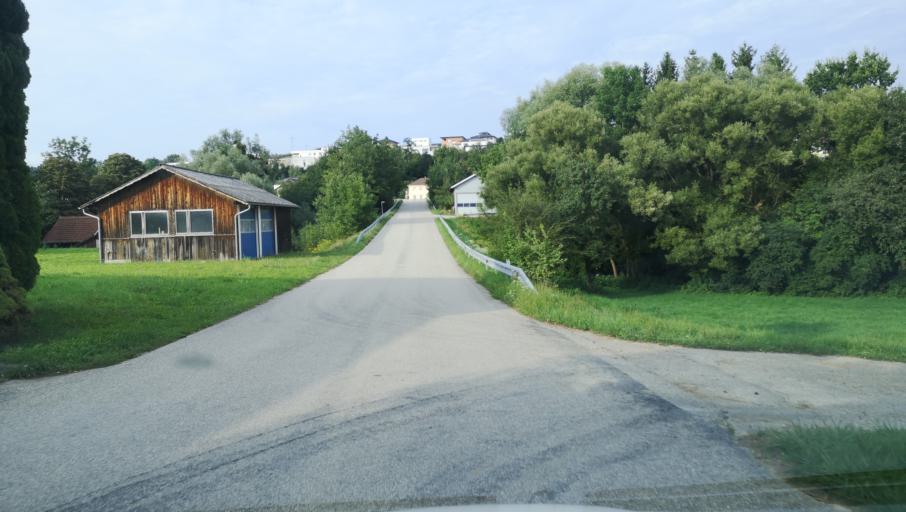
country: AT
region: Lower Austria
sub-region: Politischer Bezirk Amstetten
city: Zeillern
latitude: 48.1735
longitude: 14.8282
